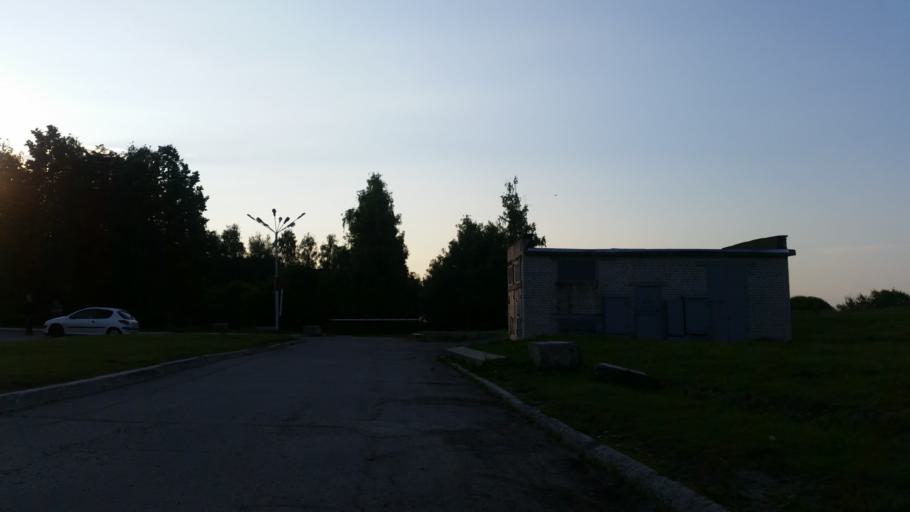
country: RU
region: Ulyanovsk
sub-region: Ulyanovskiy Rayon
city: Ulyanovsk
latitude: 54.3518
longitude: 48.3907
